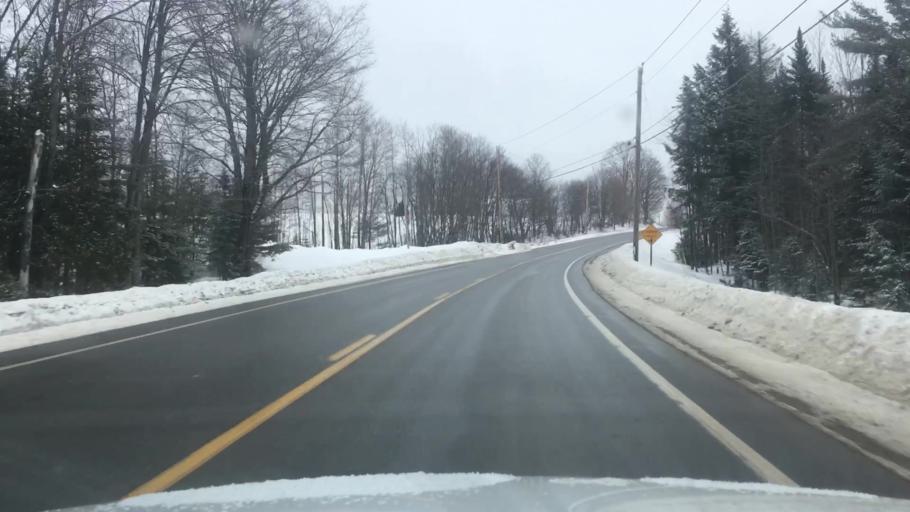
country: US
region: Maine
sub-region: Franklin County
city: Wilton
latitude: 44.5827
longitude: -70.1915
